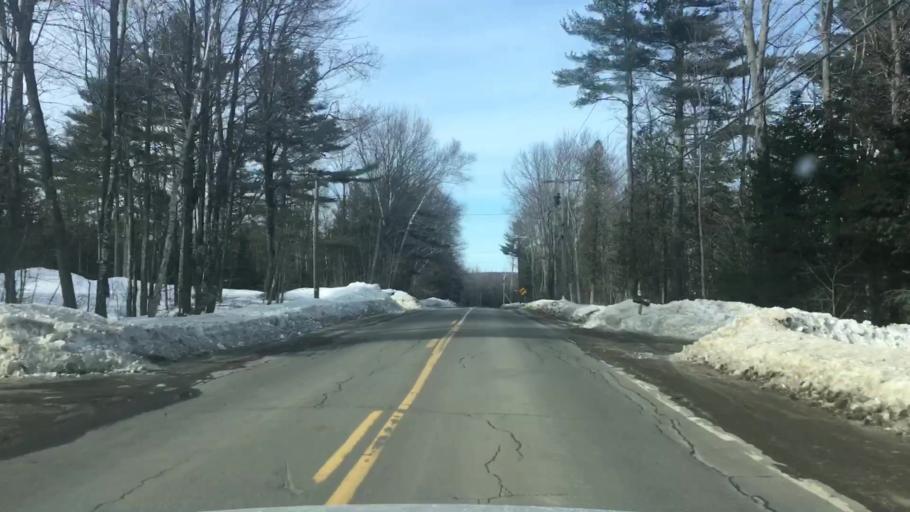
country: US
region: Maine
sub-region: Penobscot County
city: Charleston
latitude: 45.0364
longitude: -69.0327
